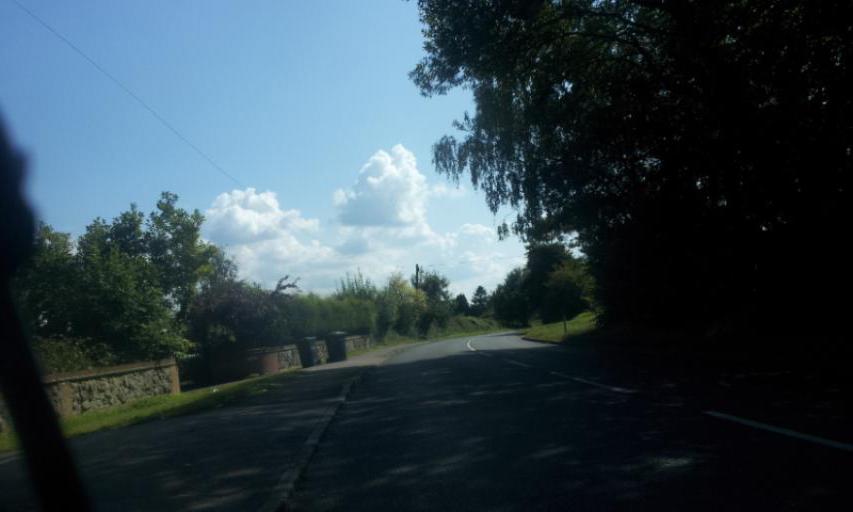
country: GB
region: England
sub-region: Kent
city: Wateringbury
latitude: 51.2645
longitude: 0.4316
